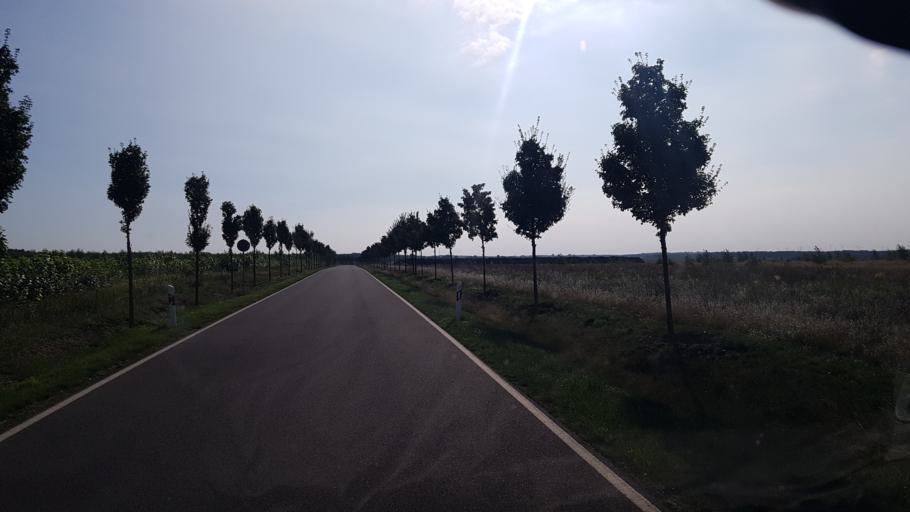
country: DE
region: Brandenburg
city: Luebben
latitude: 51.8836
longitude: 13.8165
